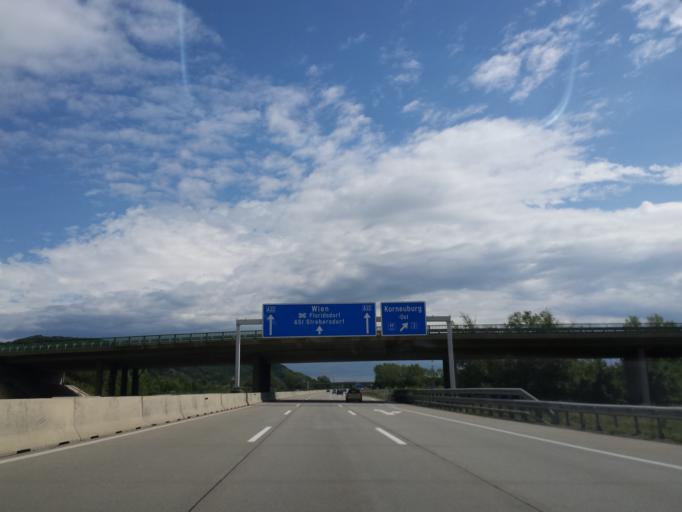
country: AT
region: Lower Austria
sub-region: Politischer Bezirk Korneuburg
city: Bisamberg
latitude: 48.3323
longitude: 16.3335
